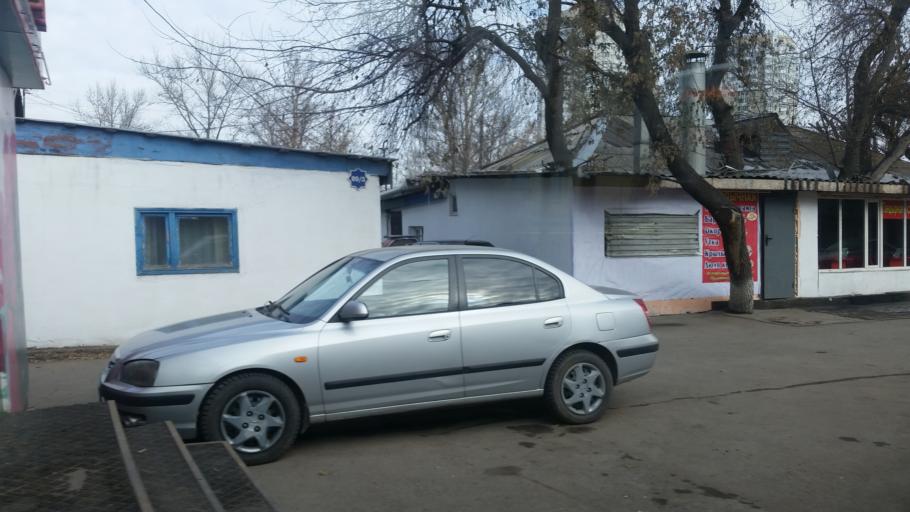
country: KZ
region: Astana Qalasy
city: Astana
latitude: 51.1630
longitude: 71.4630
